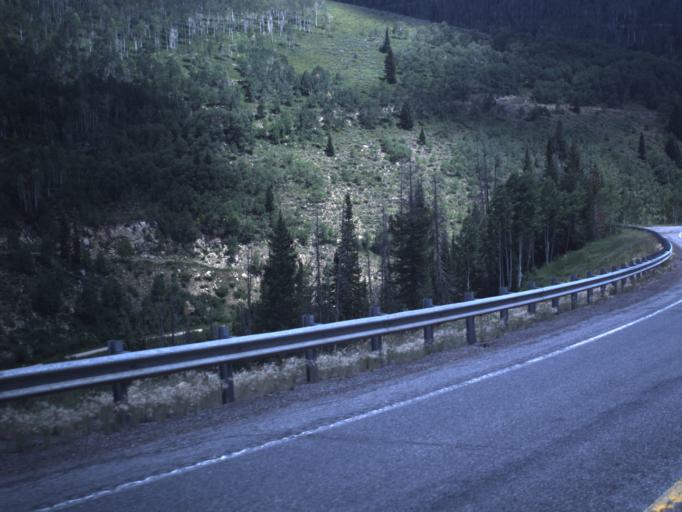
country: US
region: Utah
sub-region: Sanpete County
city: Fairview
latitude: 39.5982
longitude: -111.2097
